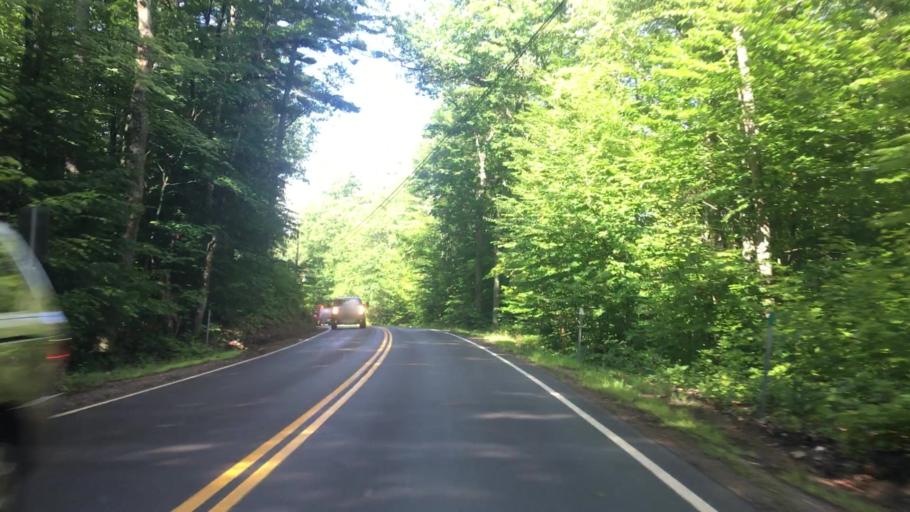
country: US
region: New Hampshire
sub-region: Belknap County
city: Gilford
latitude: 43.5402
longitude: -71.3034
